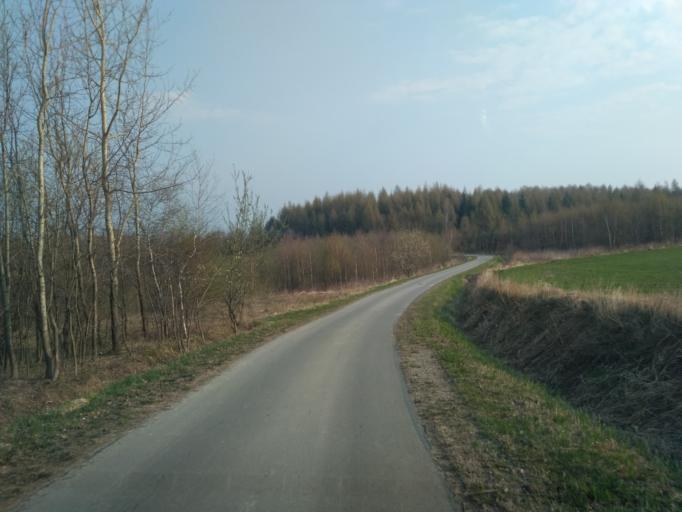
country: PL
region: Subcarpathian Voivodeship
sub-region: Powiat ropczycko-sedziszowski
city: Wielopole Skrzynskie
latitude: 49.9023
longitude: 21.6080
